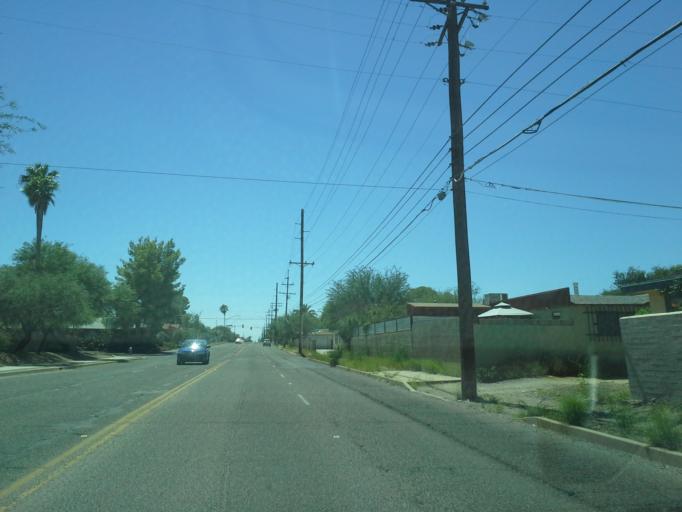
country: US
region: Arizona
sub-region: Pima County
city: Tucson
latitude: 32.2458
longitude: -110.9268
